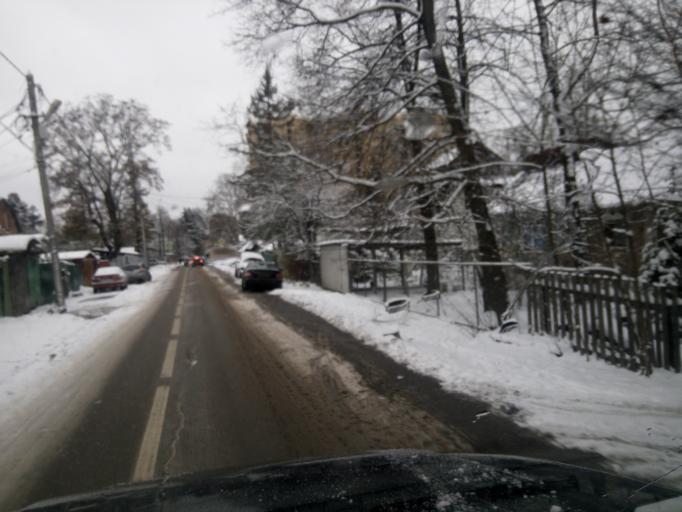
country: RU
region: Moskovskaya
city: Skhodnya
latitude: 55.9523
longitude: 37.3068
